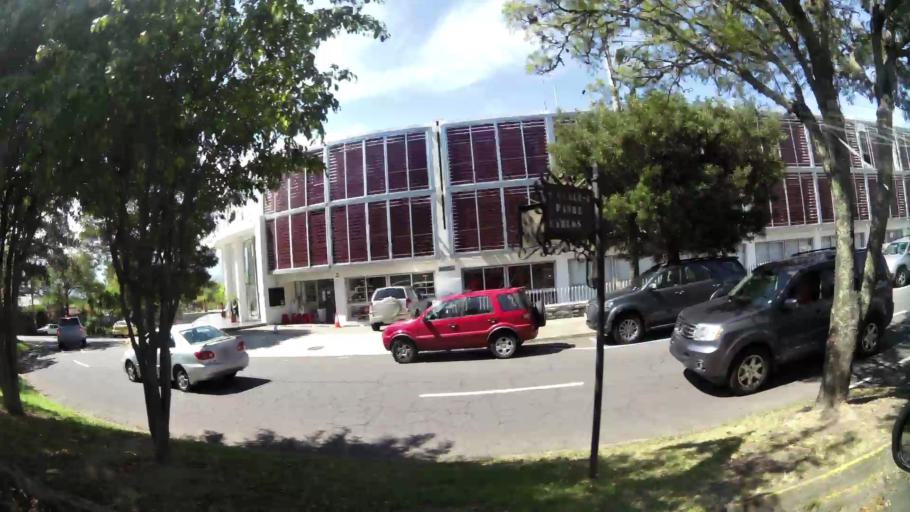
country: EC
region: Pichincha
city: Quito
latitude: -0.1954
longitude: -78.4335
